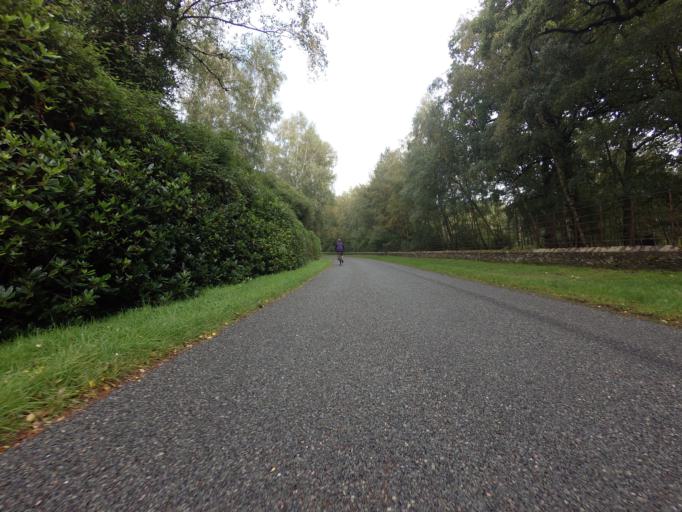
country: GB
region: England
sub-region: Norfolk
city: Dersingham
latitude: 52.8215
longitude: 0.4964
